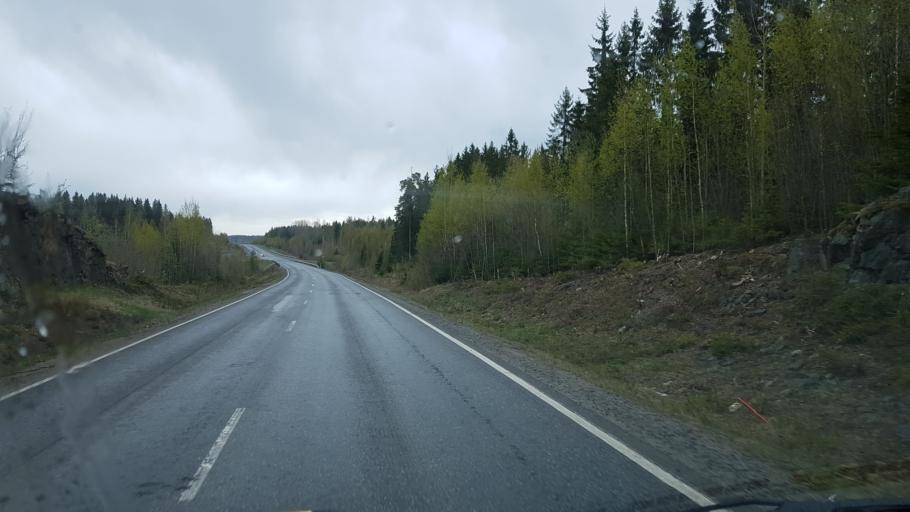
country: FI
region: Pirkanmaa
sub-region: Tampere
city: Pirkkala
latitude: 61.4069
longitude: 23.6334
